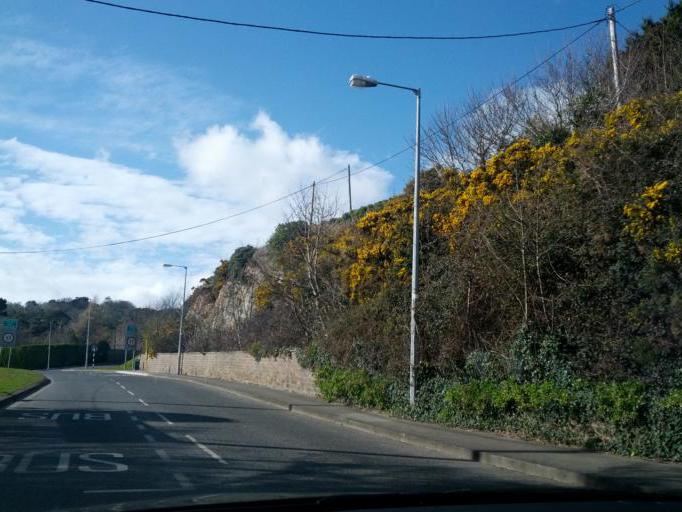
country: IE
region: Leinster
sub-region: Fingal County
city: Howth
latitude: 53.3664
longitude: -6.0655
